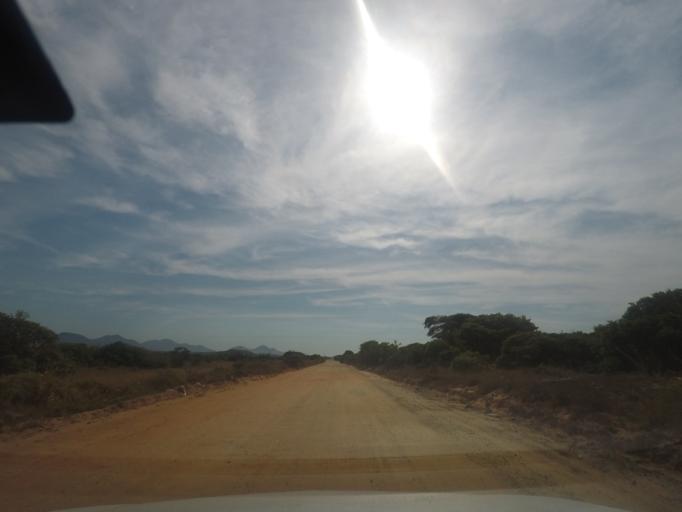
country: BR
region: Rio de Janeiro
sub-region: Marica
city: Marica
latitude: -22.9604
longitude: -42.8502
